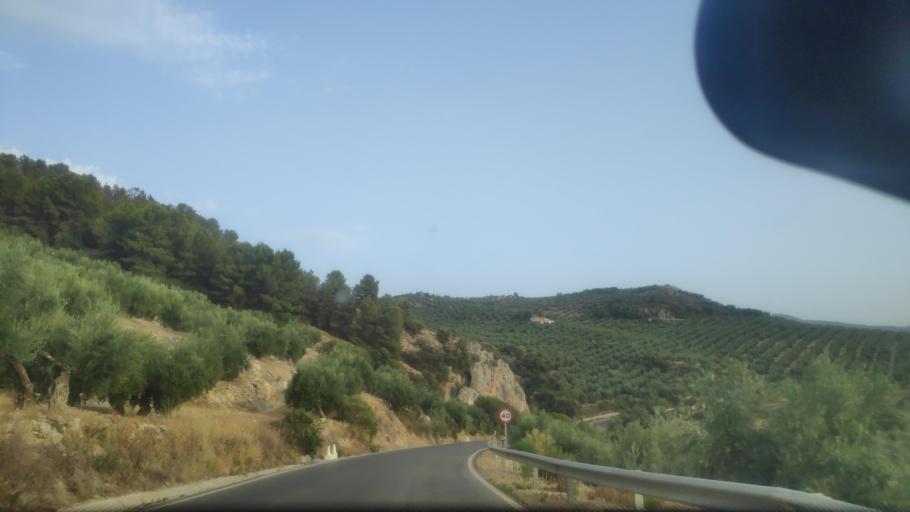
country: ES
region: Andalusia
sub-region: Provincia de Jaen
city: Torres
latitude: 37.8249
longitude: -3.5273
